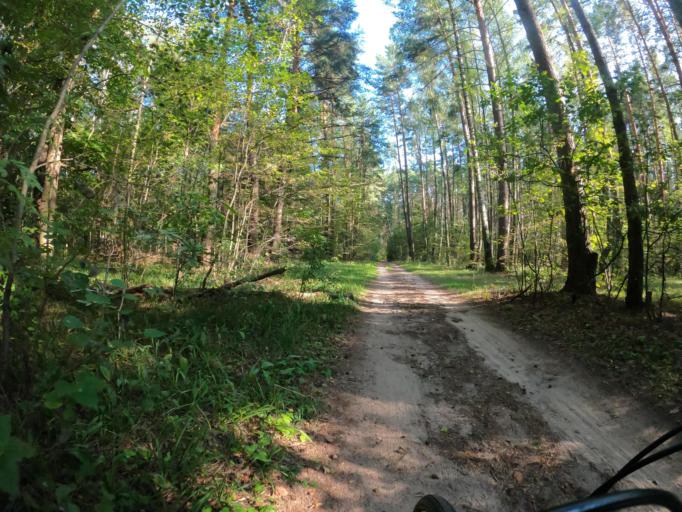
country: RU
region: Moskovskaya
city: Stupino
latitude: 54.8712
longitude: 38.0988
